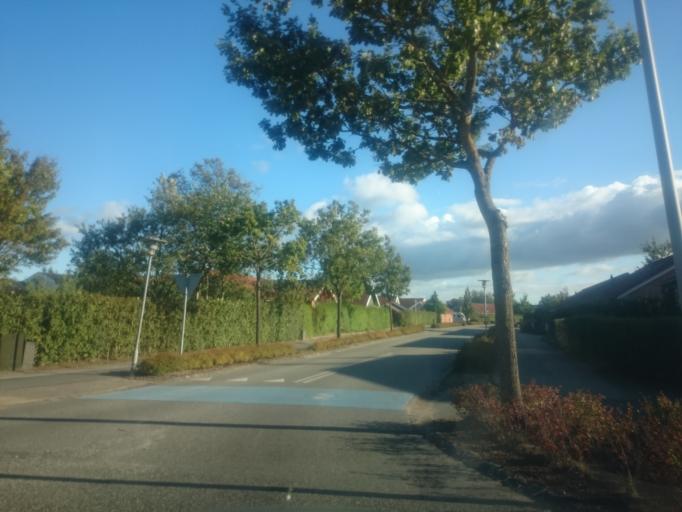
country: DK
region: South Denmark
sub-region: Billund Kommune
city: Billund
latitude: 55.7177
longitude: 9.1180
